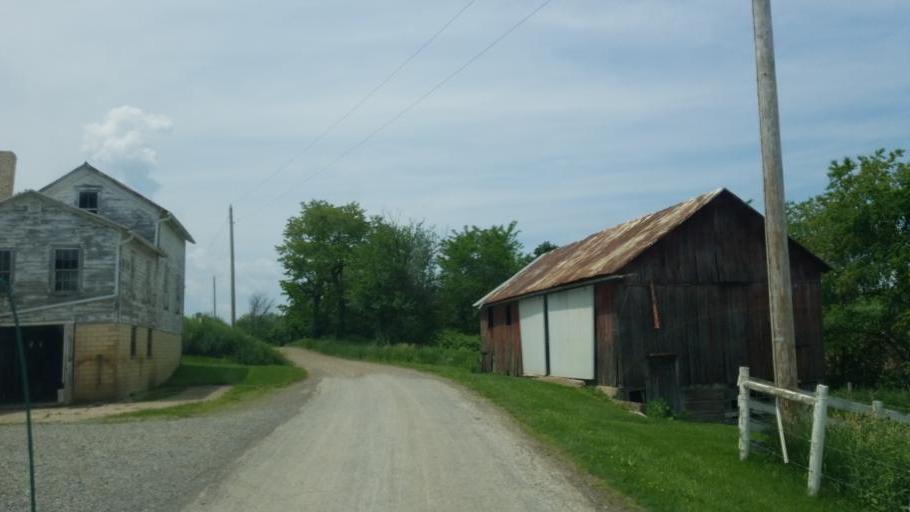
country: US
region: Ohio
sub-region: Tuscarawas County
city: Sugarcreek
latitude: 40.4728
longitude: -81.7572
